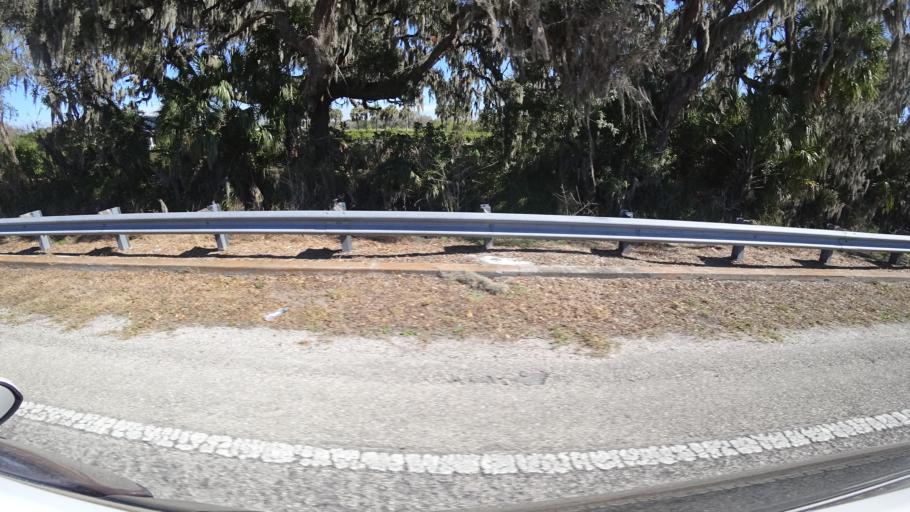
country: US
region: Florida
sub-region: Manatee County
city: Memphis
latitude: 27.5441
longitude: -82.5484
